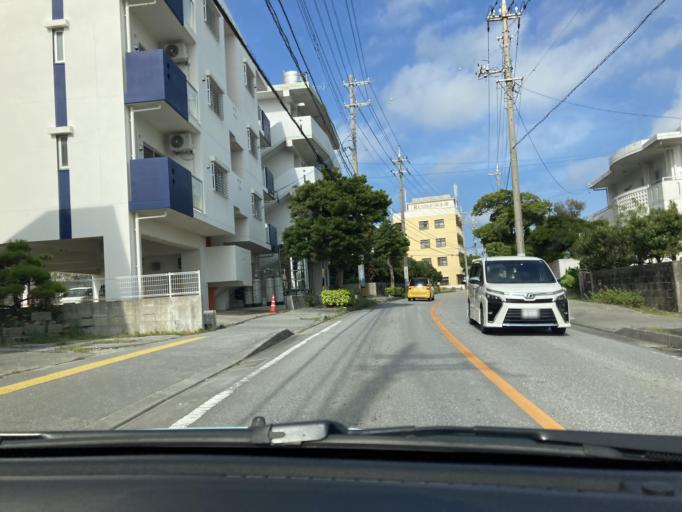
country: JP
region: Okinawa
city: Ginowan
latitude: 26.2546
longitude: 127.7731
